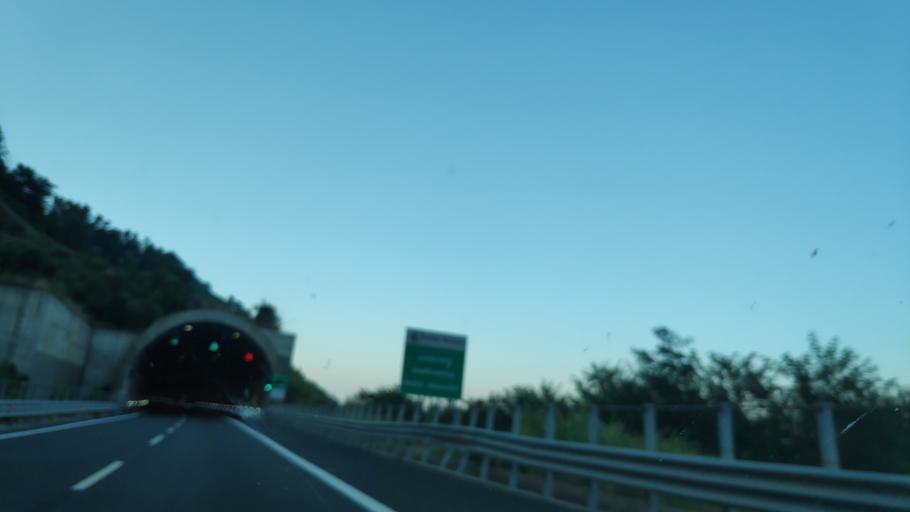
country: IT
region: Calabria
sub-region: Provincia di Reggio Calabria
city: Seminara
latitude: 38.3447
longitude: 15.8689
